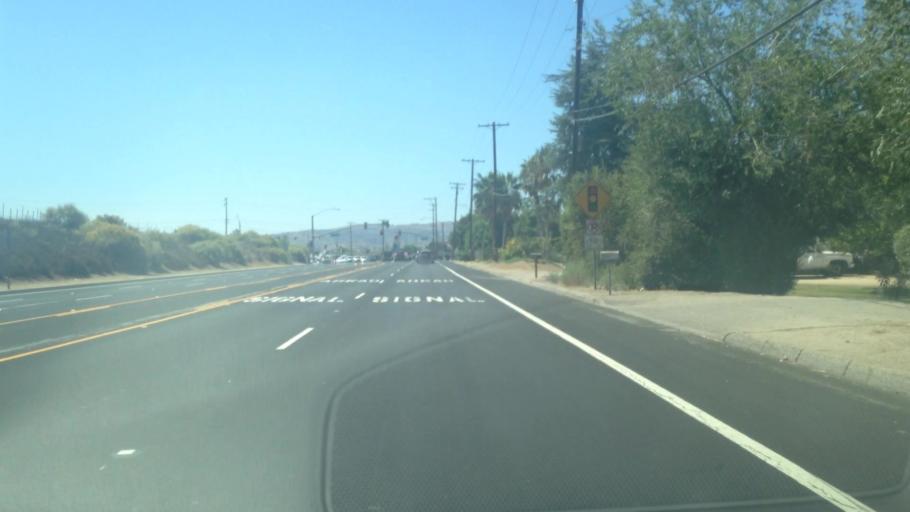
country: US
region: California
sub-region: Riverside County
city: Calimesa
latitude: 34.0188
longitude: -117.0919
